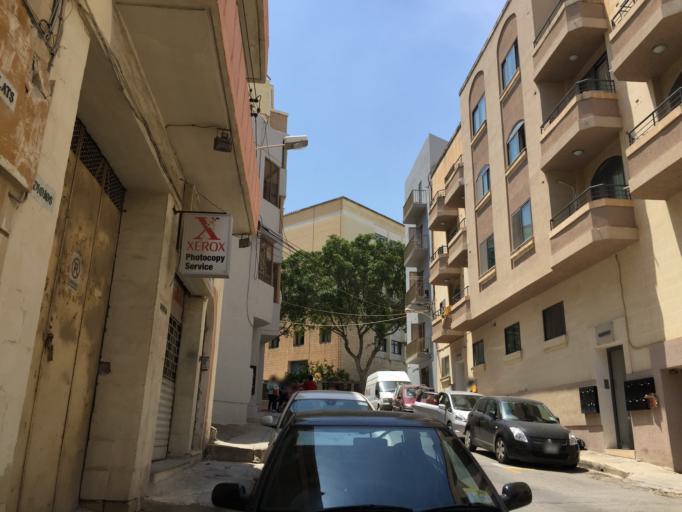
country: MT
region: Tal-Pieta
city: Pieta
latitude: 35.8935
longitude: 14.4898
